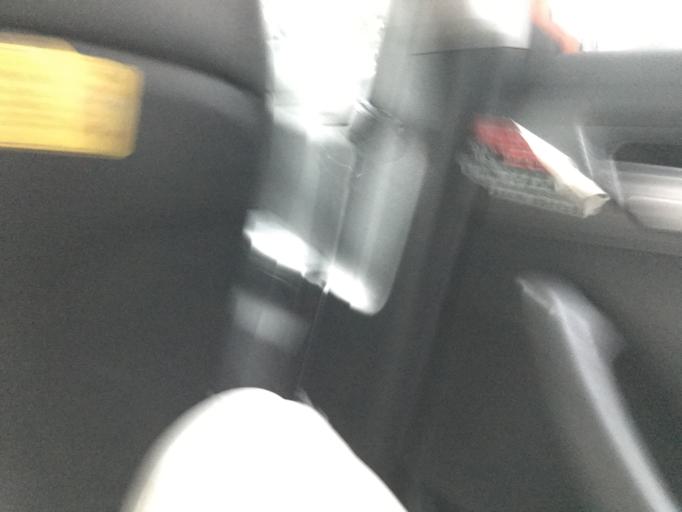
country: KR
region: Seoul
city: Seoul
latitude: 37.5695
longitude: 126.9830
